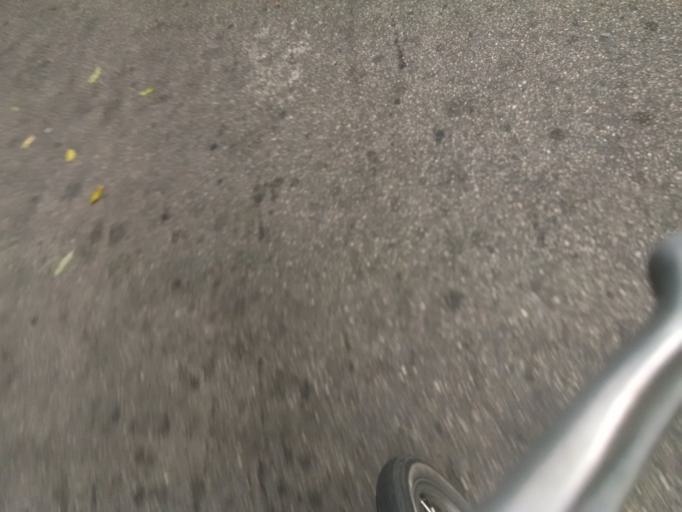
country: BR
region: Rio de Janeiro
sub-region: Rio De Janeiro
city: Rio de Janeiro
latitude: -22.9408
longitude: -43.1762
